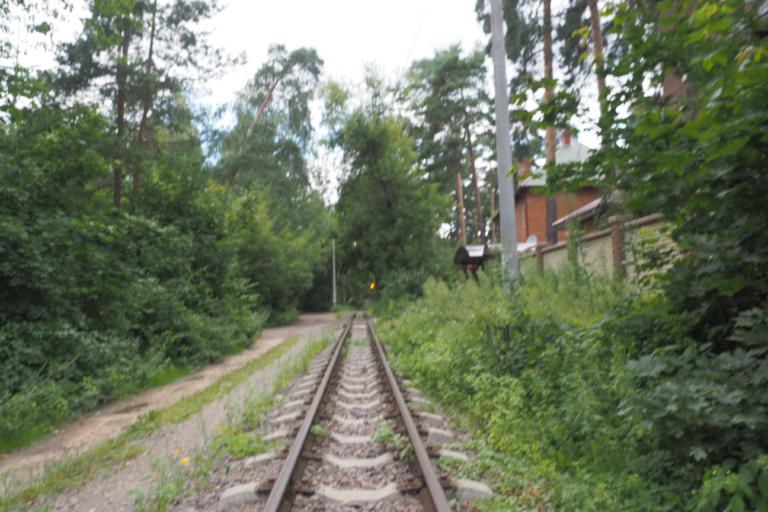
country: RU
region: Moskovskaya
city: Zhukovskiy
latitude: 55.5838
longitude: 38.1431
